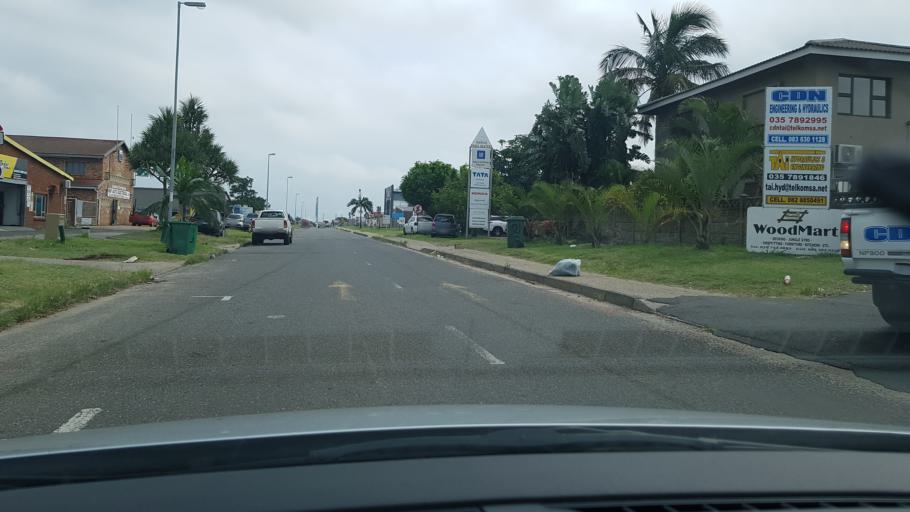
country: ZA
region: KwaZulu-Natal
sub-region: uThungulu District Municipality
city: Richards Bay
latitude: -28.7531
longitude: 32.0448
